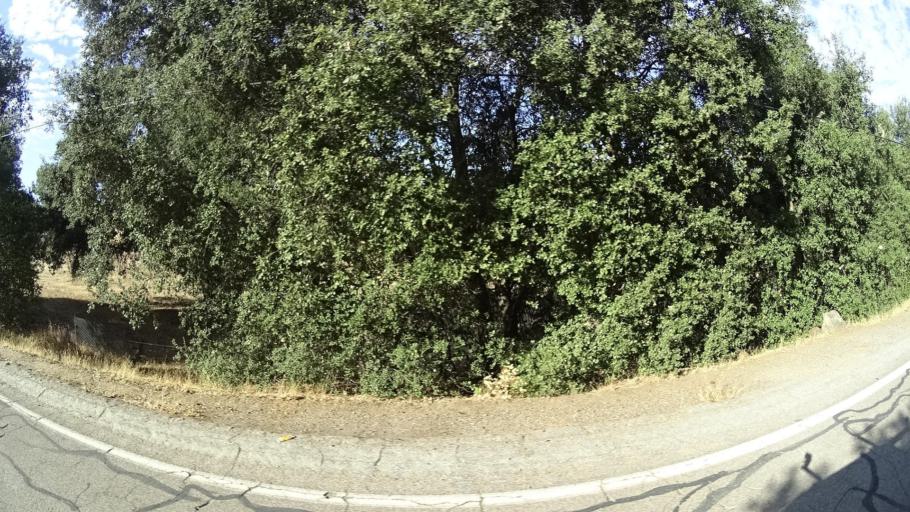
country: US
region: California
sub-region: San Diego County
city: Ramona
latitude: 33.1858
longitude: -116.7776
